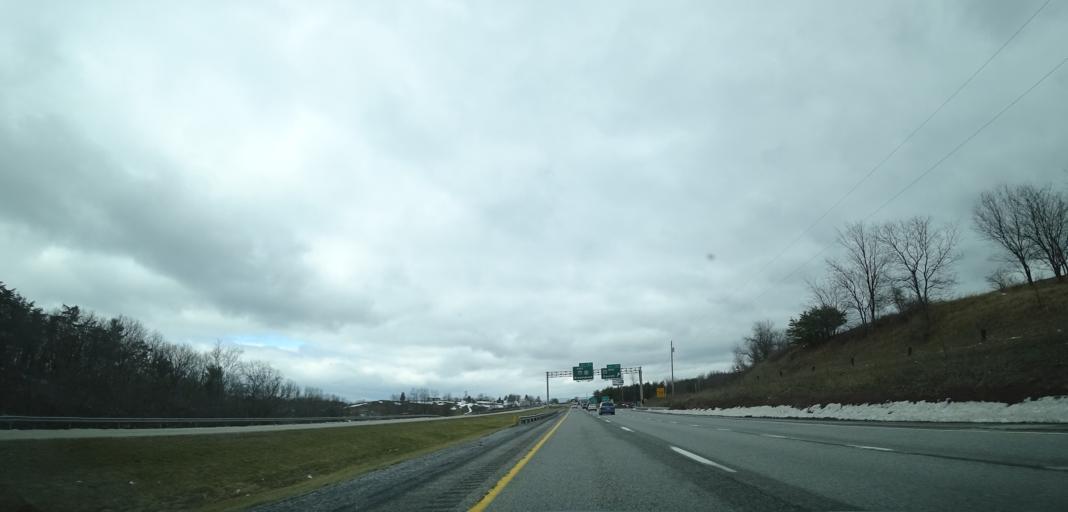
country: US
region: Pennsylvania
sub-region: Bedford County
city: Earlston
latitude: 39.9763
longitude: -78.2450
